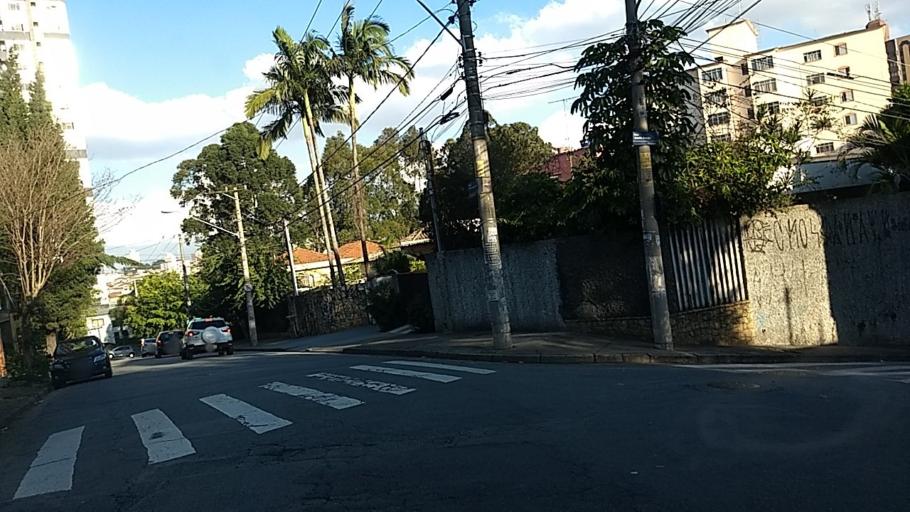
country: BR
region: Sao Paulo
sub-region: Sao Paulo
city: Sao Paulo
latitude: -23.4900
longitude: -46.6124
